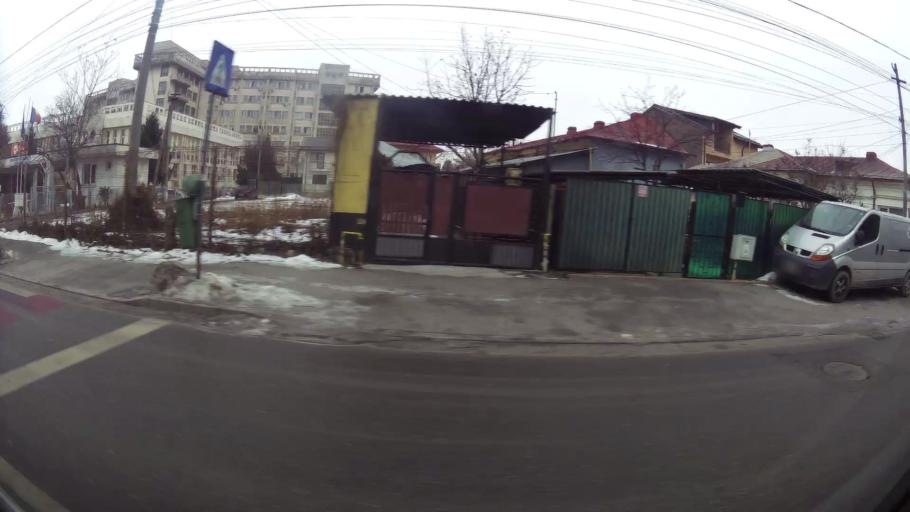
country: RO
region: Prahova
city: Ploiesti
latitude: 44.9398
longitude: 26.0393
